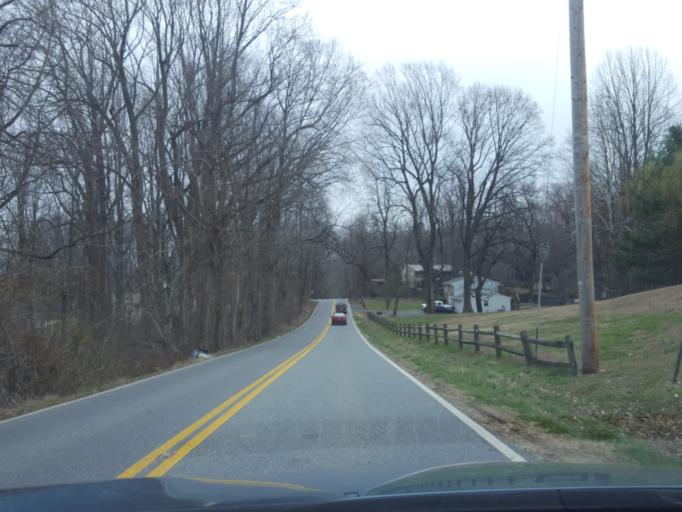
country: US
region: Maryland
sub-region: Calvert County
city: North Beach
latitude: 38.7128
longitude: -76.5538
